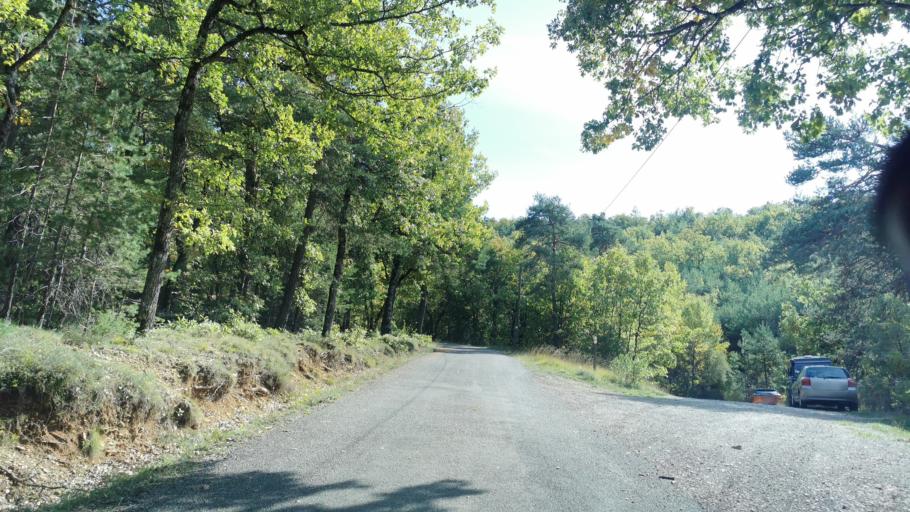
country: FR
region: Provence-Alpes-Cote d'Azur
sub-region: Departement des Alpes-de-Haute-Provence
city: Volonne
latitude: 44.1813
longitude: 6.0265
